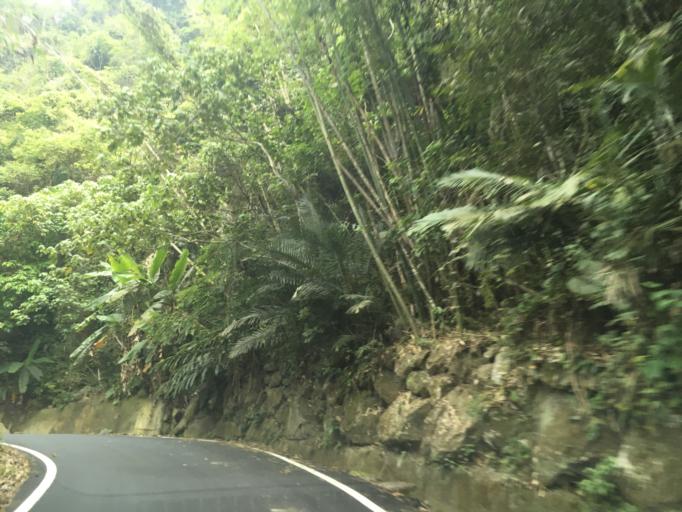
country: TW
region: Taiwan
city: Zhongxing New Village
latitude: 23.9861
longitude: 120.8115
